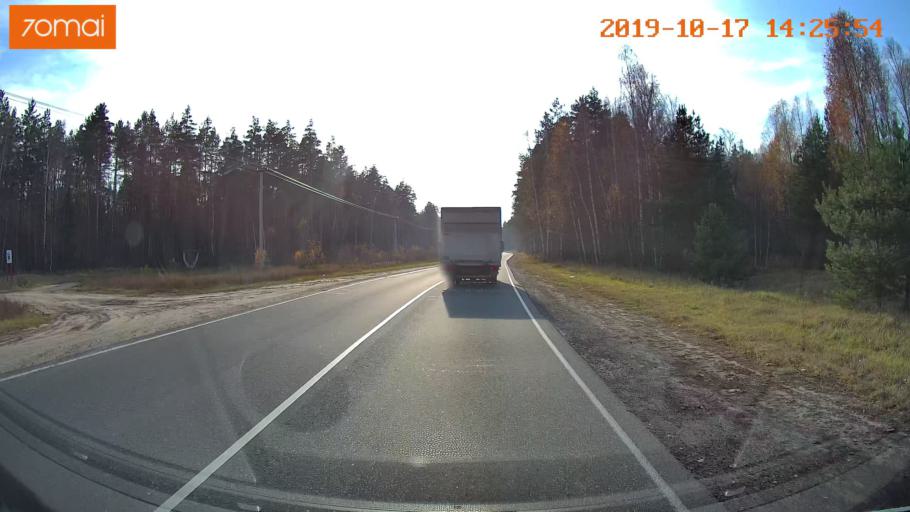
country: RU
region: Moskovskaya
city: Radovitskiy
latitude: 54.9962
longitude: 39.9738
